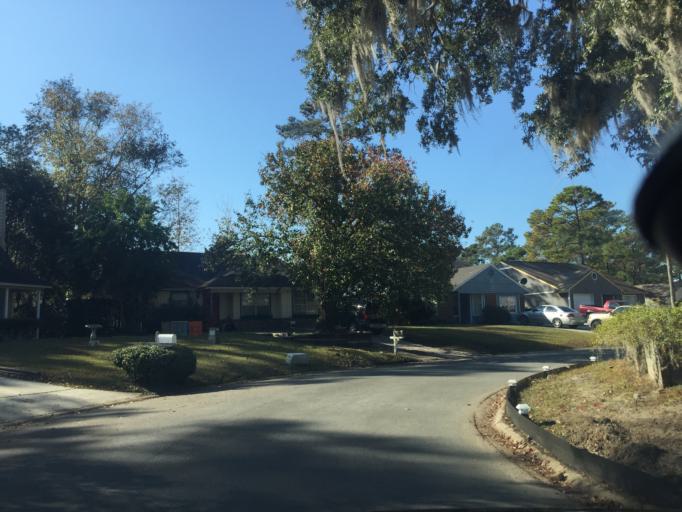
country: US
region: Georgia
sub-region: Chatham County
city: Montgomery
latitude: 31.9985
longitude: -81.1388
